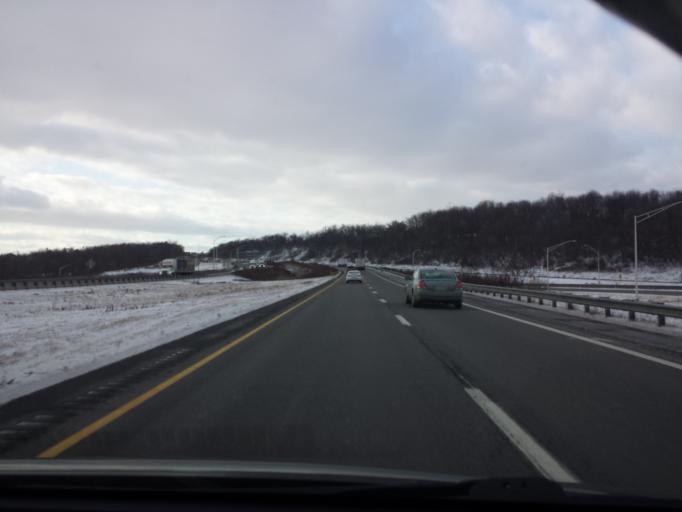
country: US
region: Pennsylvania
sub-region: Columbia County
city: Mifflinville
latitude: 41.0339
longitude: -76.3360
